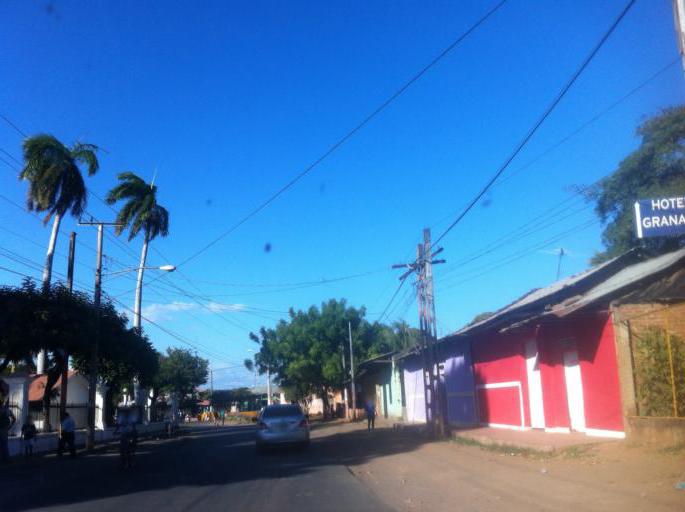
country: NI
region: Granada
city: Granada
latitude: 11.9224
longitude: -85.9646
